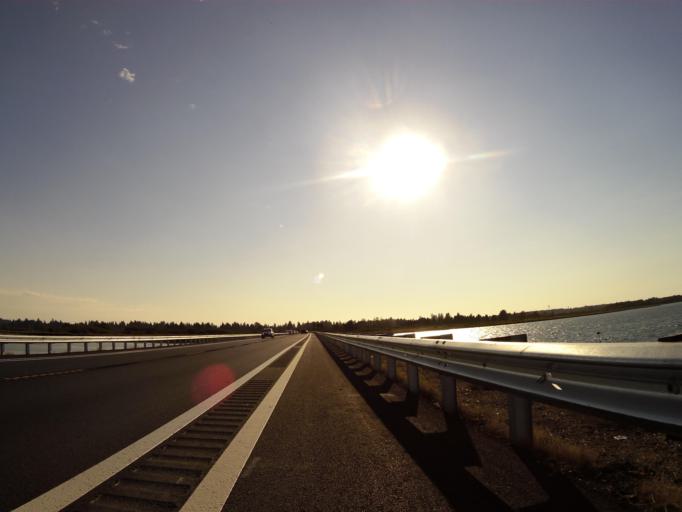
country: US
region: Oregon
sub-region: Clatsop County
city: Warrenton
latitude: 46.1684
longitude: -123.8863
